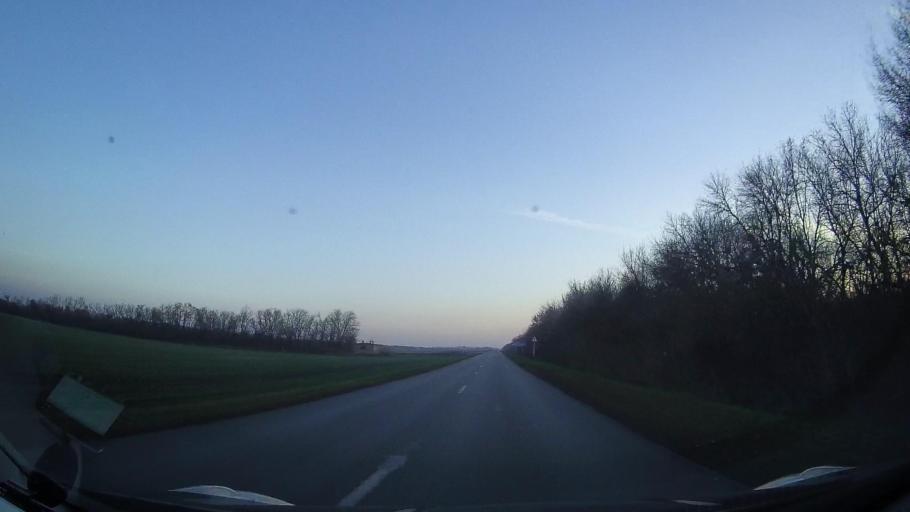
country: RU
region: Rostov
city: Zernograd
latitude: 47.0305
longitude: 40.3917
